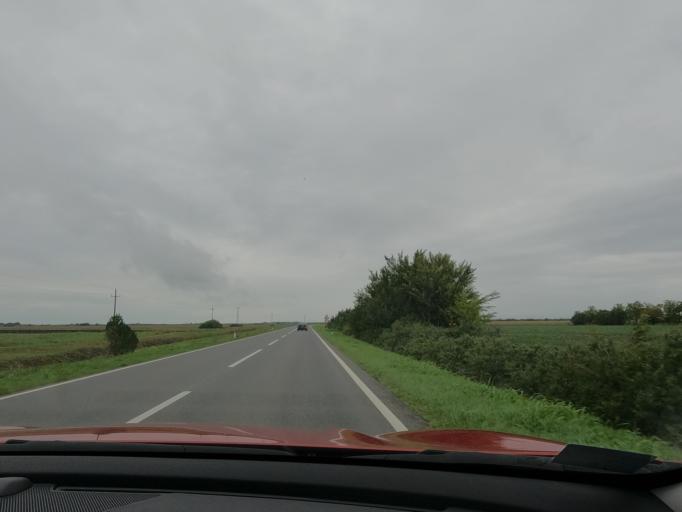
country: RS
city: Banatska Topola
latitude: 45.7099
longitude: 20.4182
